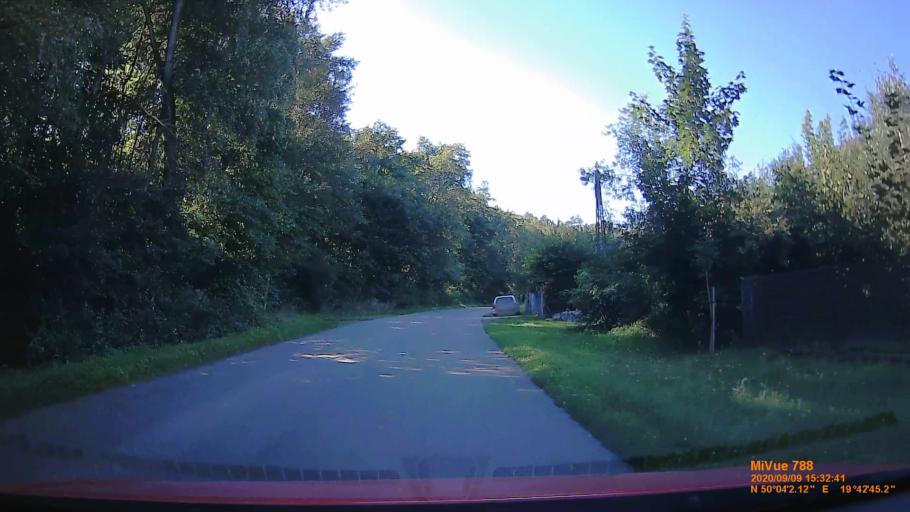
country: PL
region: Lesser Poland Voivodeship
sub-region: Powiat krakowski
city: Czulow
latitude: 50.0673
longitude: 19.7126
